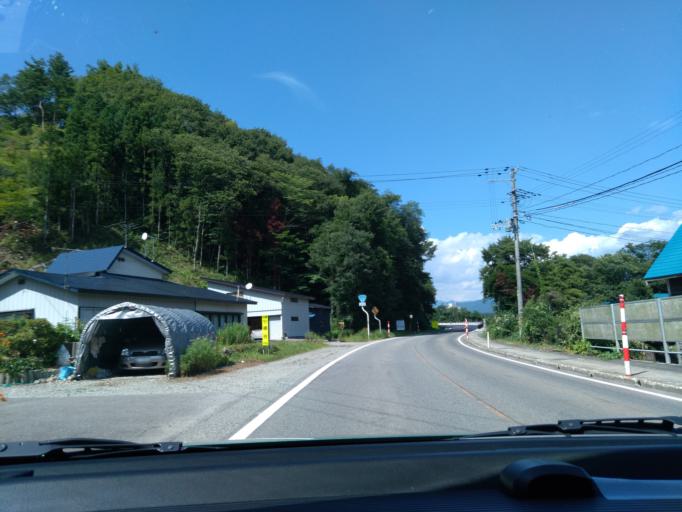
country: JP
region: Akita
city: Kakunodatemachi
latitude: 39.6833
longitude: 140.7070
